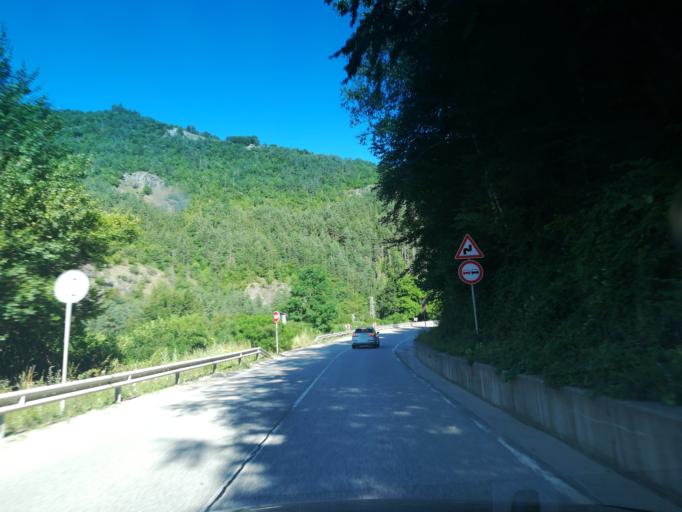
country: BG
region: Smolyan
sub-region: Obshtina Chepelare
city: Chepelare
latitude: 41.8262
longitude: 24.6907
